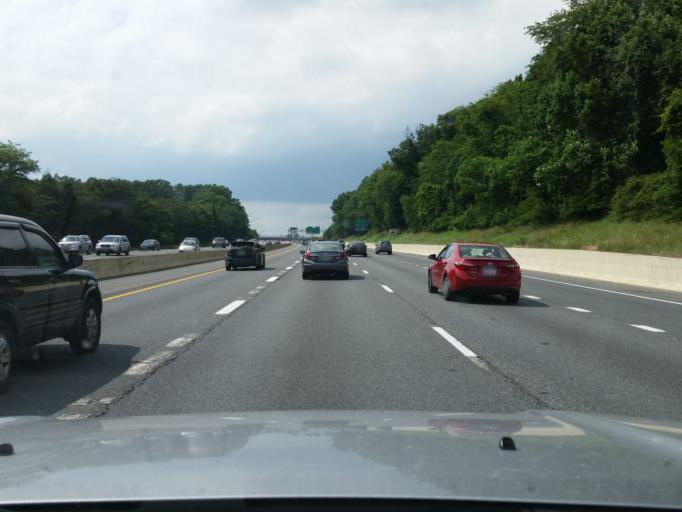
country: US
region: Maryland
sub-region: Montgomery County
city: Germantown
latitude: 39.1776
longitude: -77.2486
